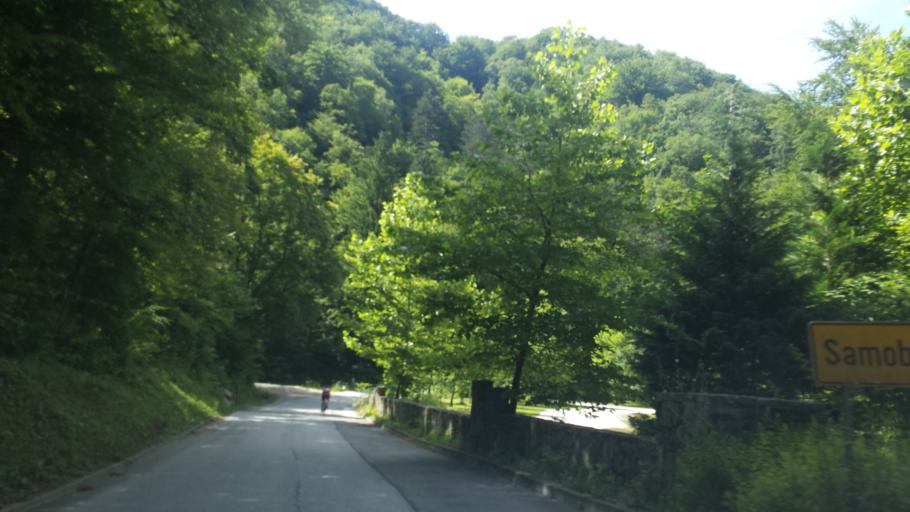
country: HR
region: Zagrebacka
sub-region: Grad Samobor
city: Samobor
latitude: 45.7937
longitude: 15.6913
